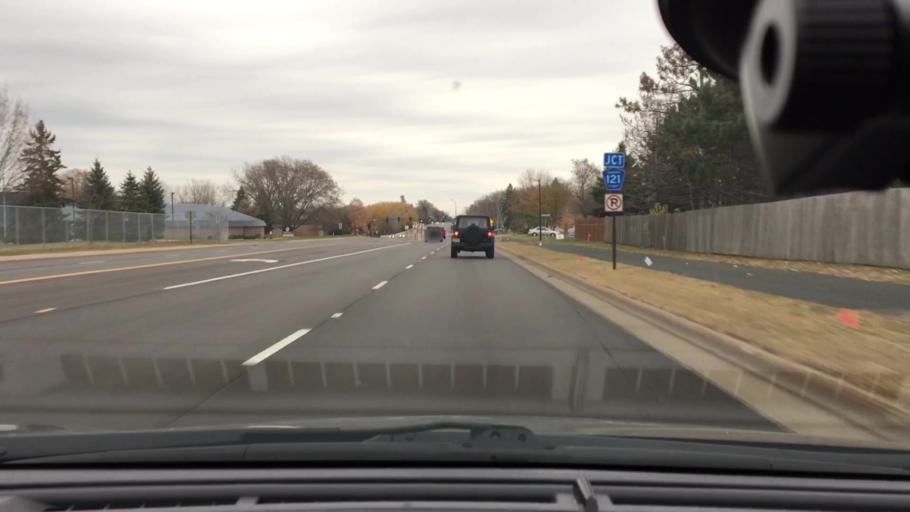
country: US
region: Minnesota
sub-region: Hennepin County
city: Maple Grove
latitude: 45.1234
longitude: -93.4655
